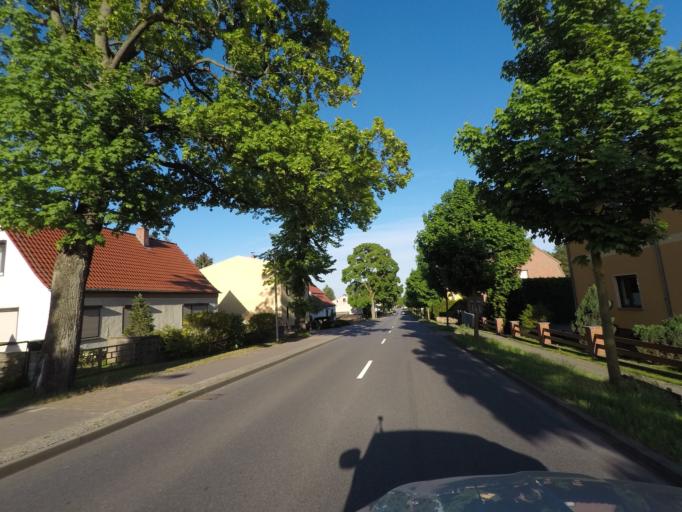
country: DE
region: Brandenburg
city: Eberswalde
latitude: 52.8257
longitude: 13.8578
